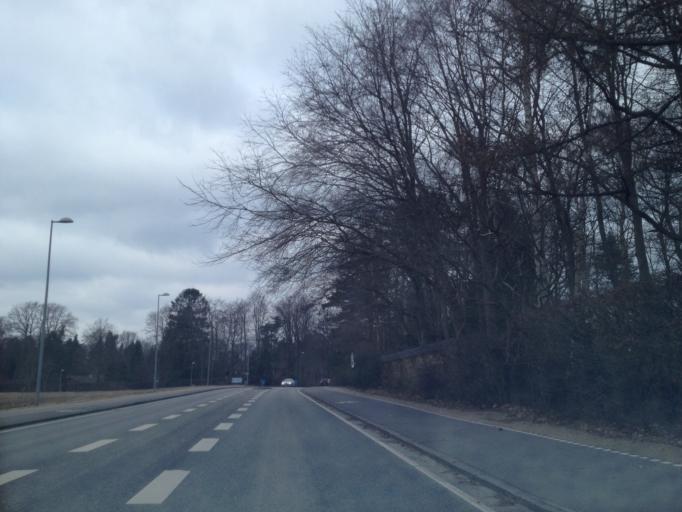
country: DK
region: Capital Region
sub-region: Rudersdal Kommune
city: Trorod
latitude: 55.8667
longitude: 12.5513
